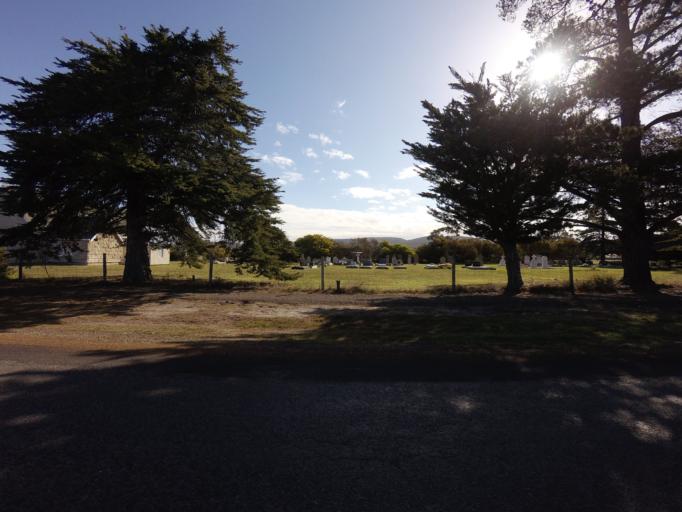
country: AU
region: Tasmania
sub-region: Sorell
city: Sorell
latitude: -42.5032
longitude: 147.9155
